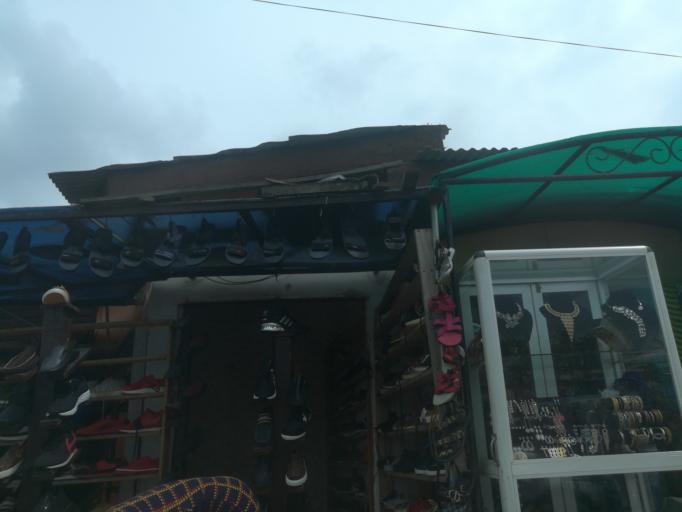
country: NG
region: Lagos
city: Ikeja
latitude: 6.5931
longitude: 3.3380
